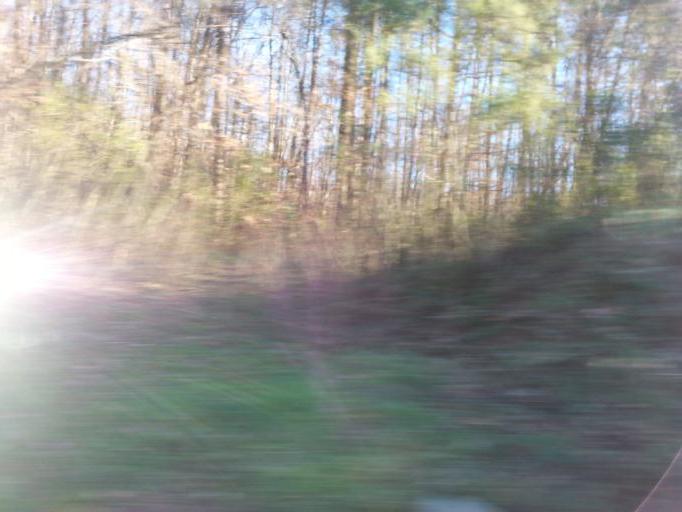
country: US
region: Tennessee
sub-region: Anderson County
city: Oak Ridge
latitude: 36.0815
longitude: -84.2481
